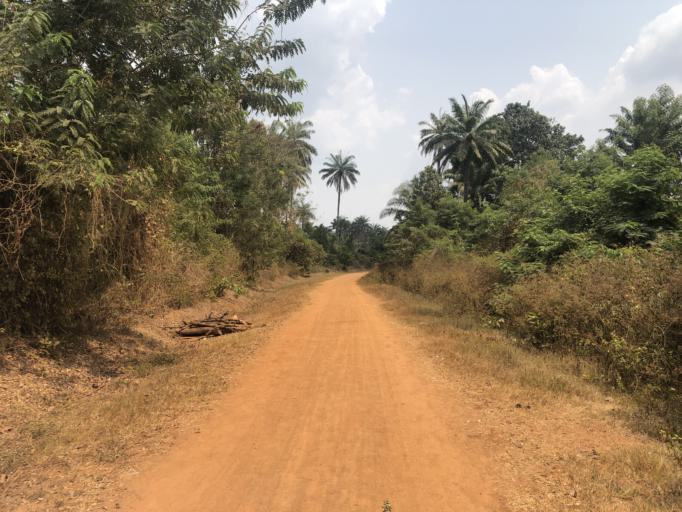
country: NG
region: Osun
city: Bode Osi
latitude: 7.7613
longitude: 4.2723
